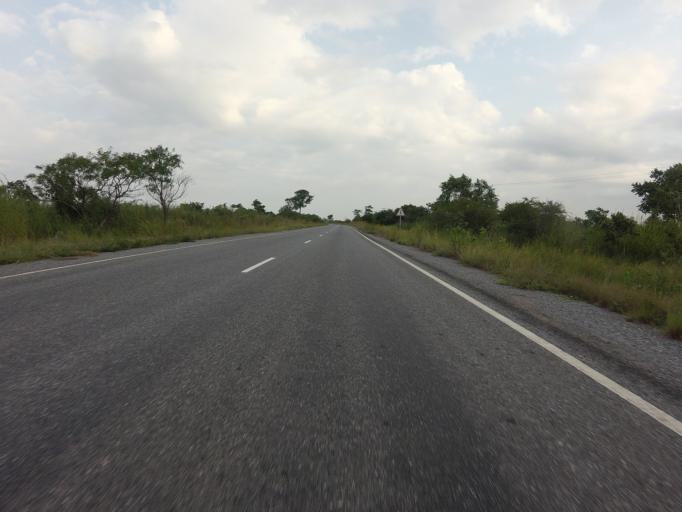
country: GH
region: Volta
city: Ho
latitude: 6.3390
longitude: 0.5404
